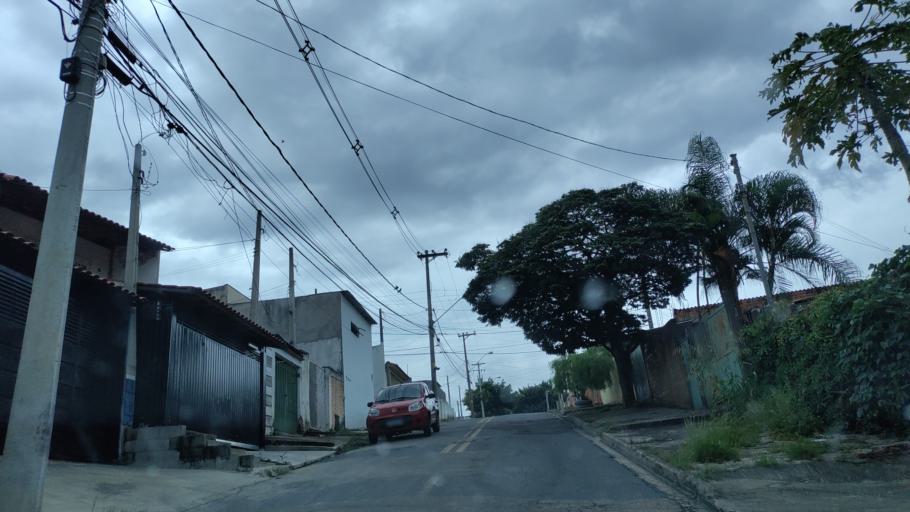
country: BR
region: Sao Paulo
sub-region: Sorocaba
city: Sorocaba
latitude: -23.4697
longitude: -47.4694
